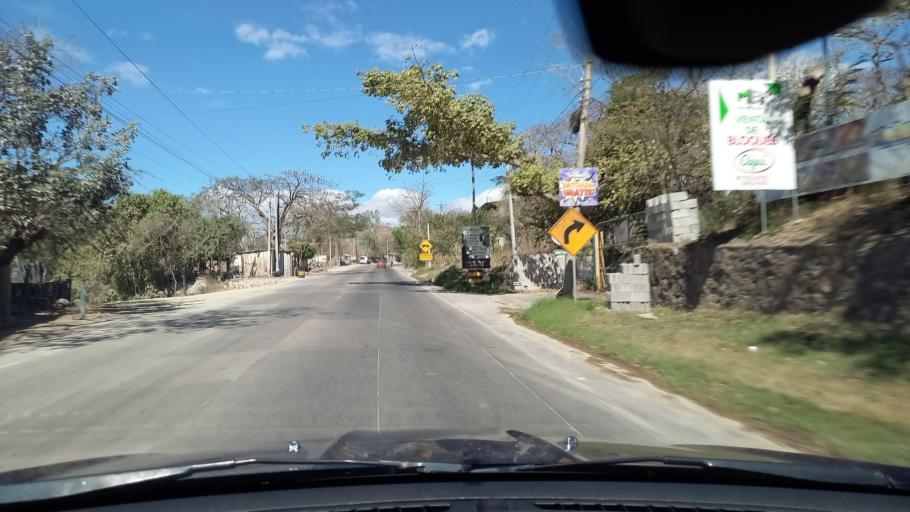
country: SV
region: Santa Ana
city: Metapan
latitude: 14.3417
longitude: -89.4523
